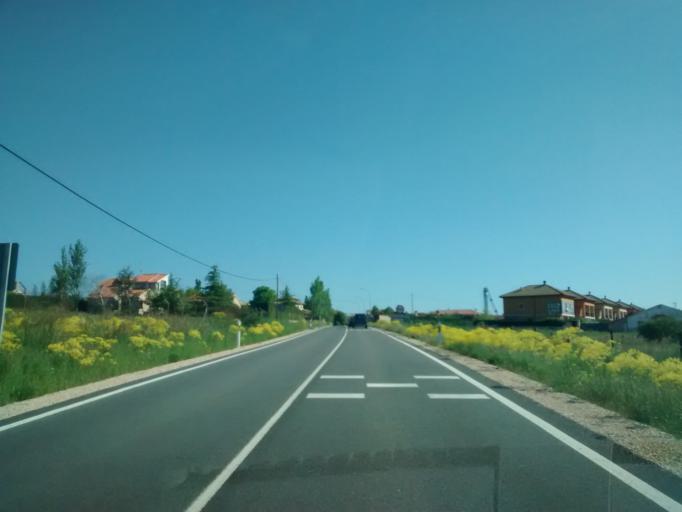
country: ES
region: Castille and Leon
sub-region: Provincia de Segovia
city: Torrecaballeros
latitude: 40.9884
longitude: -4.0238
